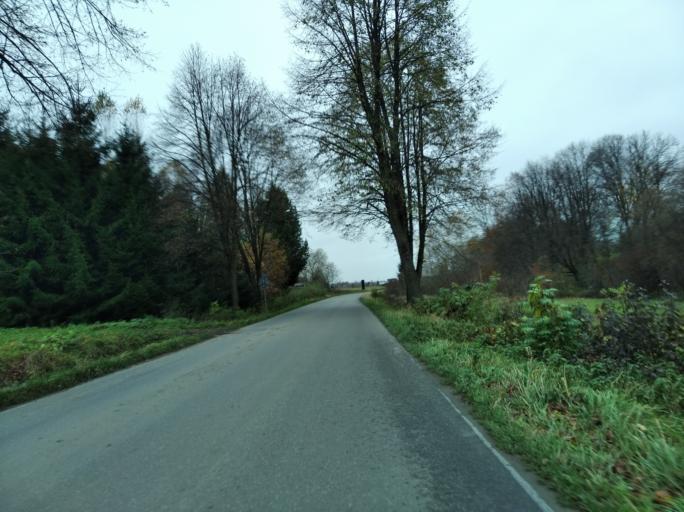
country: PL
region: Subcarpathian Voivodeship
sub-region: Powiat krosnienski
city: Chorkowka
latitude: 49.6763
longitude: 21.6809
